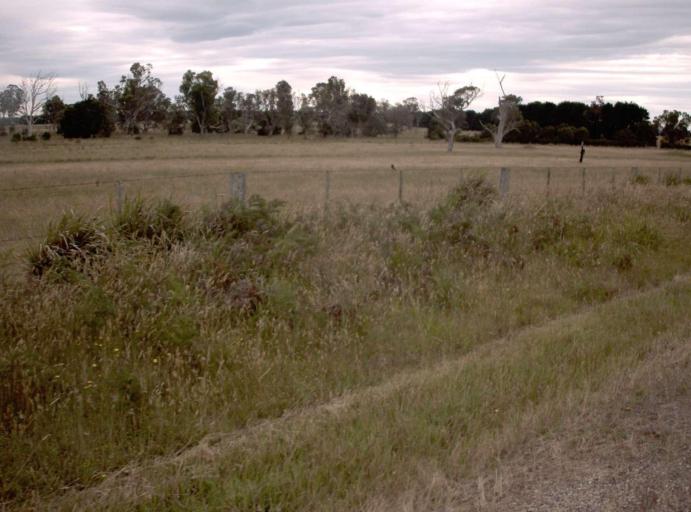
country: AU
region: Victoria
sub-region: East Gippsland
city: Bairnsdale
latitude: -37.9692
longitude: 147.4779
